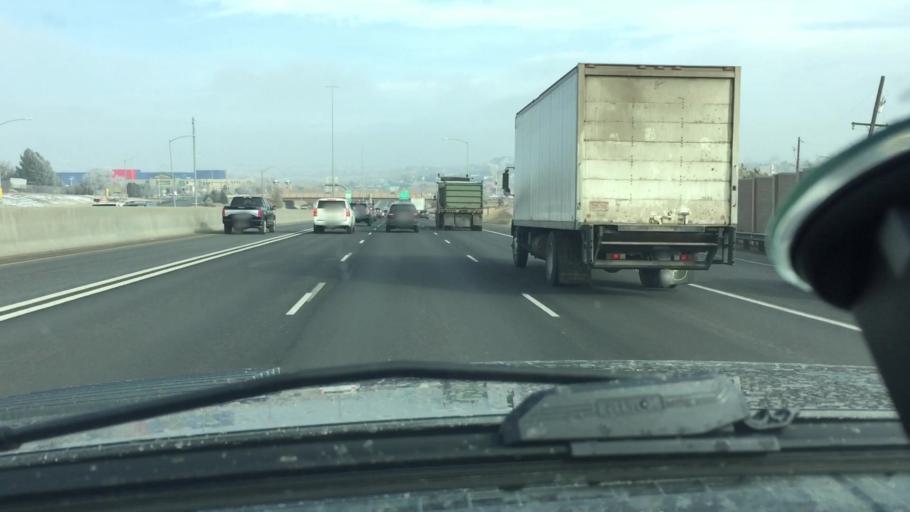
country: US
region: Colorado
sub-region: Adams County
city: Federal Heights
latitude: 39.8445
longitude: -104.9862
